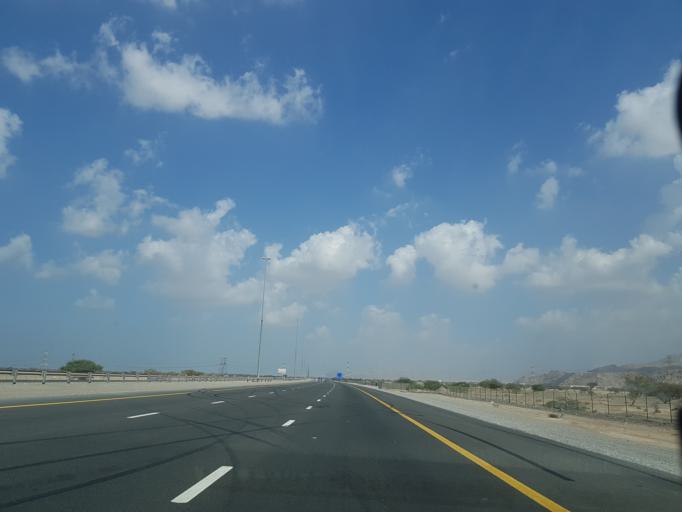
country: AE
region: Ra's al Khaymah
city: Ras al-Khaimah
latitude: 25.7342
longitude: 56.0151
